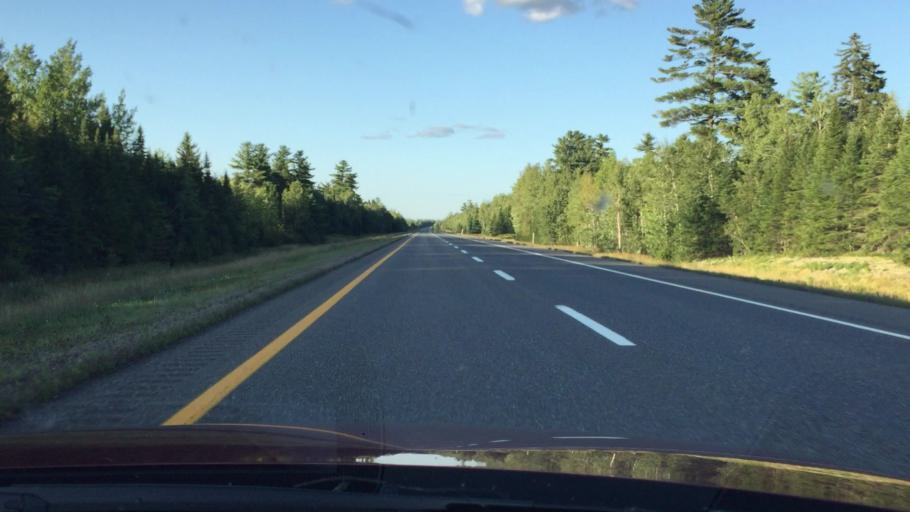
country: US
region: Maine
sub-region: Penobscot County
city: Patten
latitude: 46.0692
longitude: -68.2243
